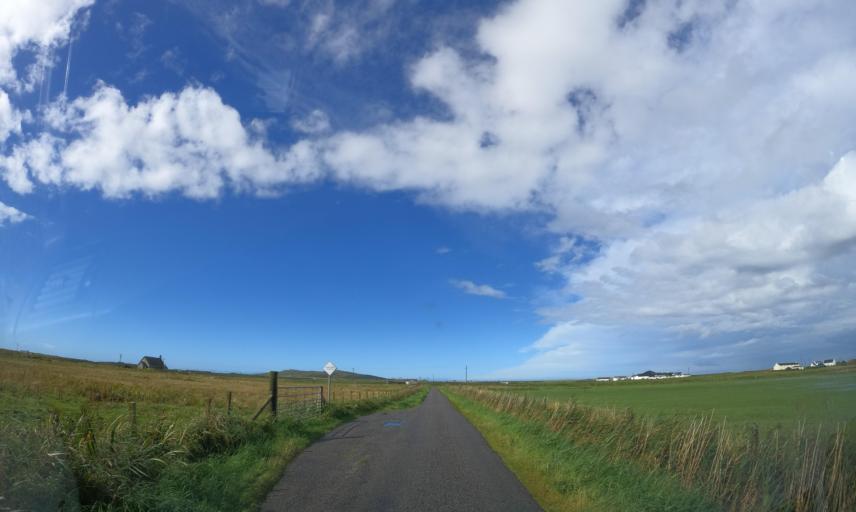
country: GB
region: Scotland
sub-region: Eilean Siar
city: Barra
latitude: 56.5207
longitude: -6.9094
